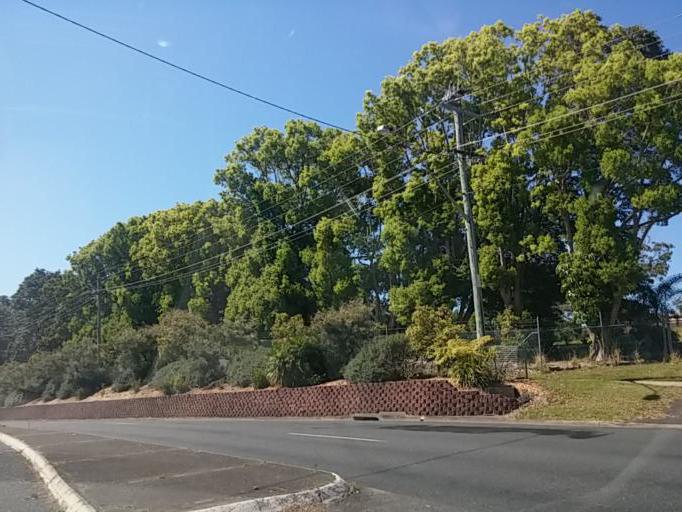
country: AU
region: New South Wales
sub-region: Coffs Harbour
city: Coffs Harbour
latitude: -30.3049
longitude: 153.1272
